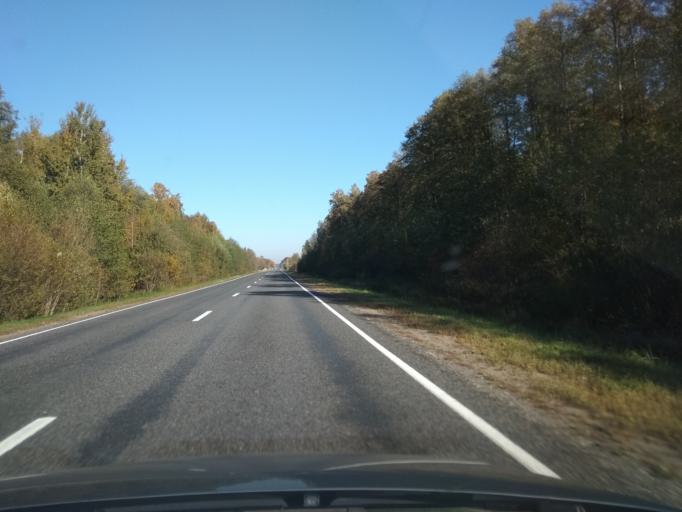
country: BY
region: Brest
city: Malaryta
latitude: 51.9792
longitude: 24.2021
